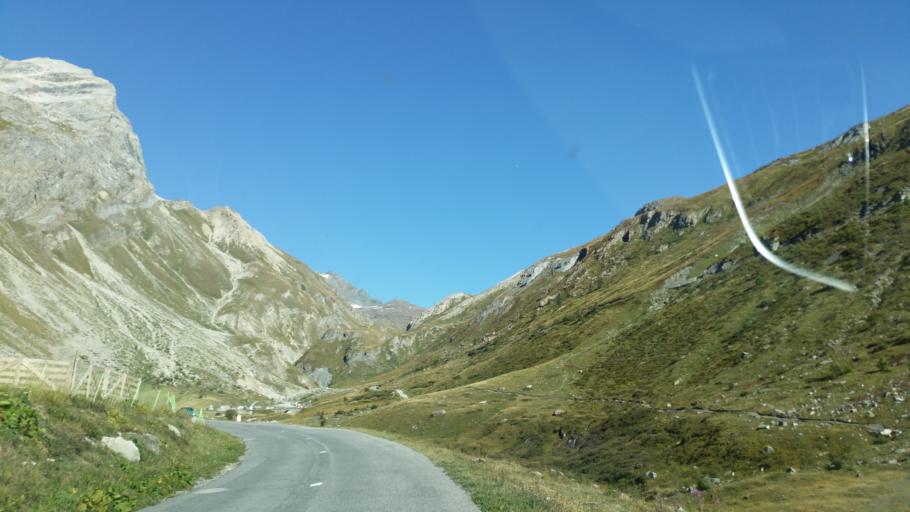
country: FR
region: Rhone-Alpes
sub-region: Departement de la Savoie
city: Val-d'Isere
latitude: 45.4526
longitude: 7.0283
